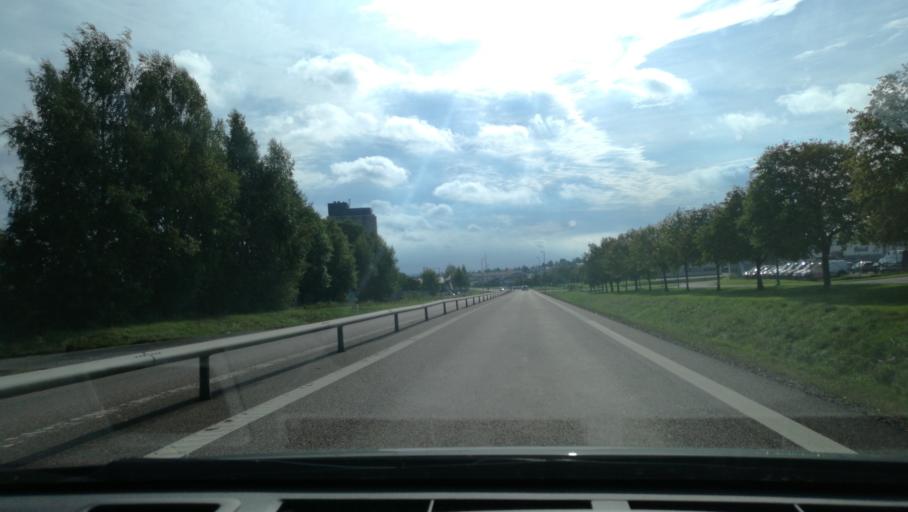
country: SE
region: Dalarna
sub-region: Hedemora Kommun
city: Hedemora
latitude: 60.2918
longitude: 15.9836
